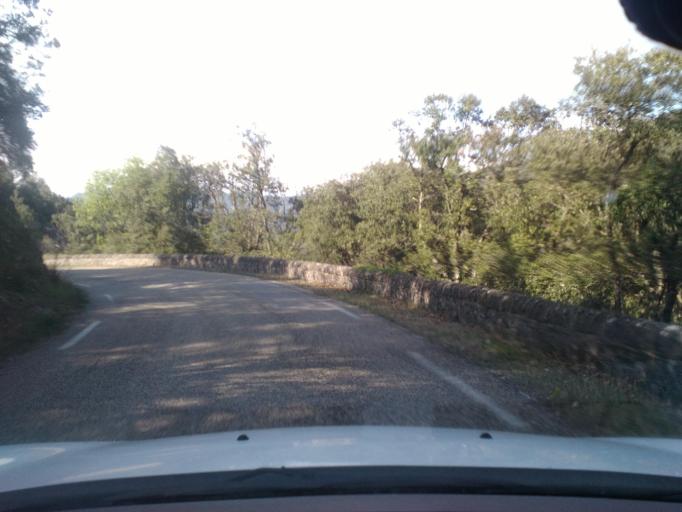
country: FR
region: Languedoc-Roussillon
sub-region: Departement du Gard
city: Lasalle
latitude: 44.0806
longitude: 3.8162
